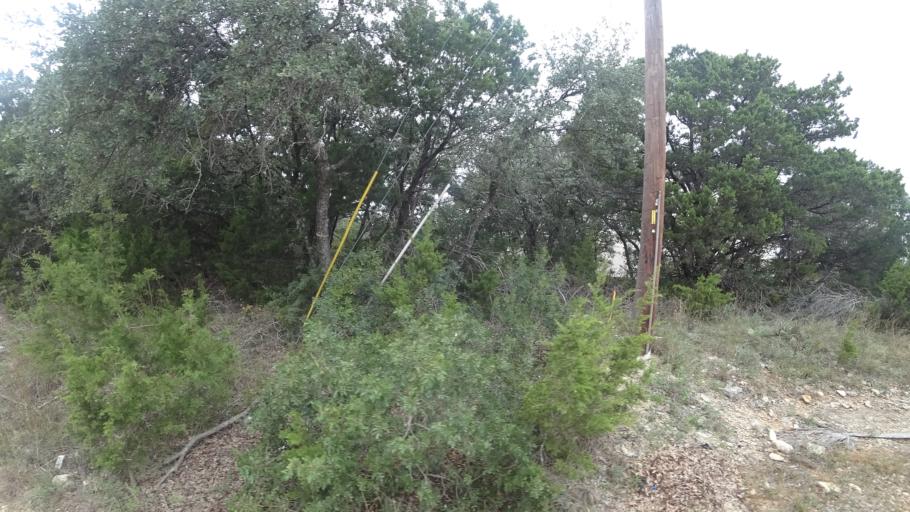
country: US
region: Texas
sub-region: Travis County
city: Hudson Bend
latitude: 30.3876
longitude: -97.9402
